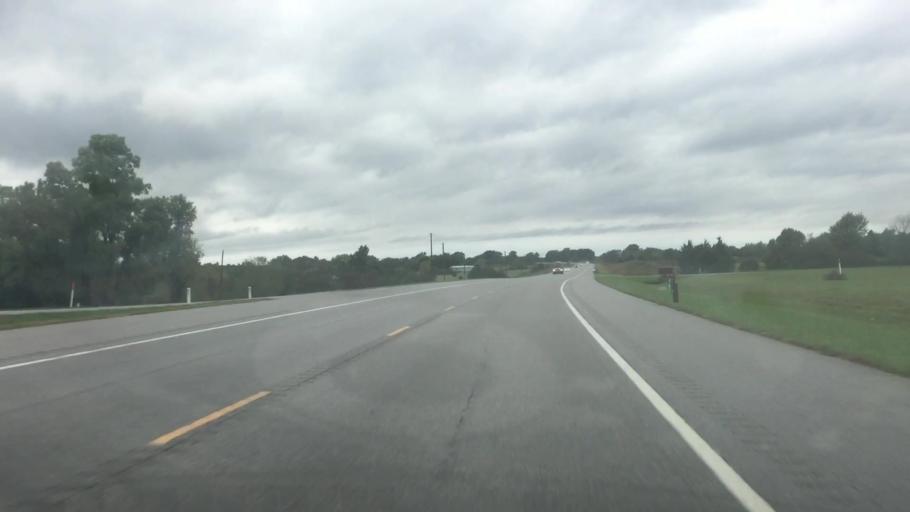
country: US
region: Kansas
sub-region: Miami County
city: Osawatomie
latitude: 38.4450
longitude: -94.9855
